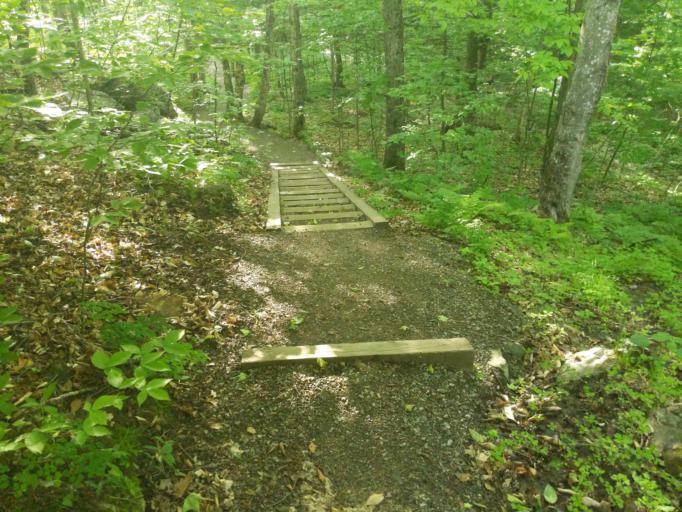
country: CA
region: Quebec
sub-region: Outaouais
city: Wakefield
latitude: 45.5095
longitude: -75.9128
